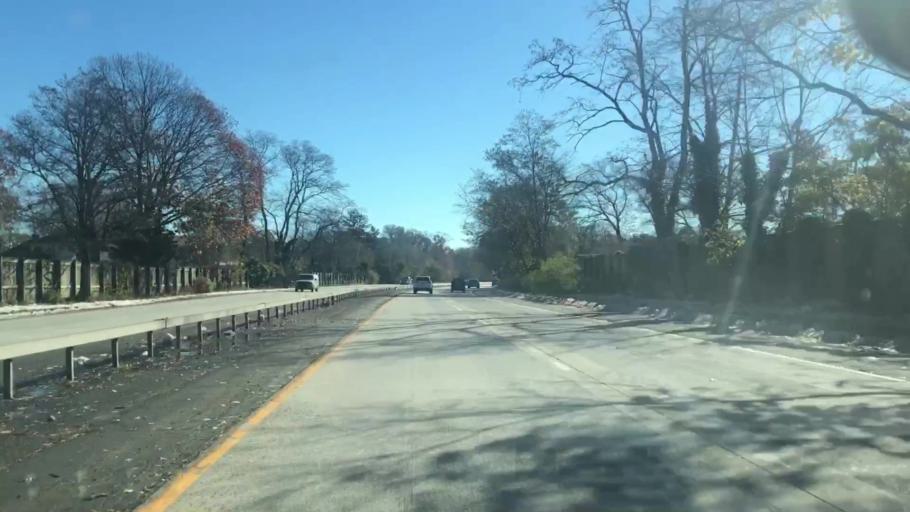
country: US
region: New York
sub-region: Suffolk County
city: North Babylon
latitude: 40.7259
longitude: -73.3176
